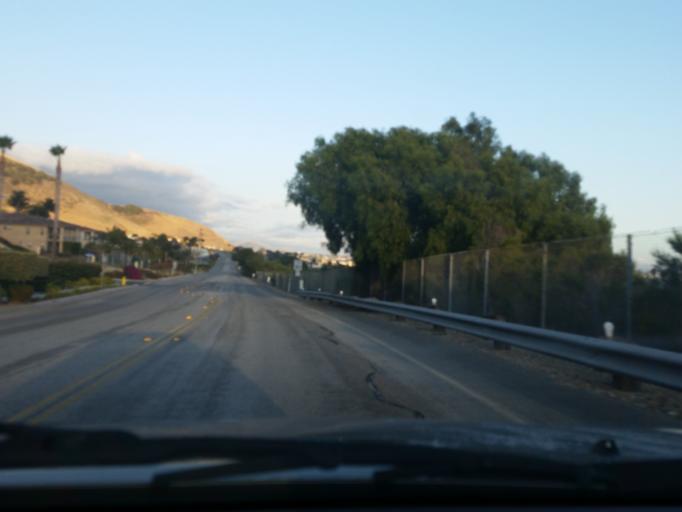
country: US
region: California
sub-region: San Luis Obispo County
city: Pismo Beach
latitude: 35.1595
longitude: -120.6750
